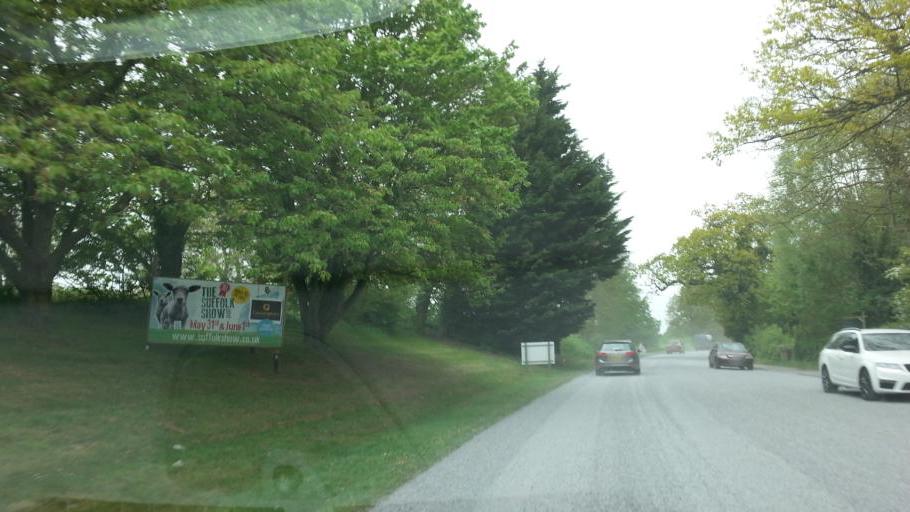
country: GB
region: England
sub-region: Suffolk
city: Bury St Edmunds
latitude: 52.2028
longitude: 0.7569
